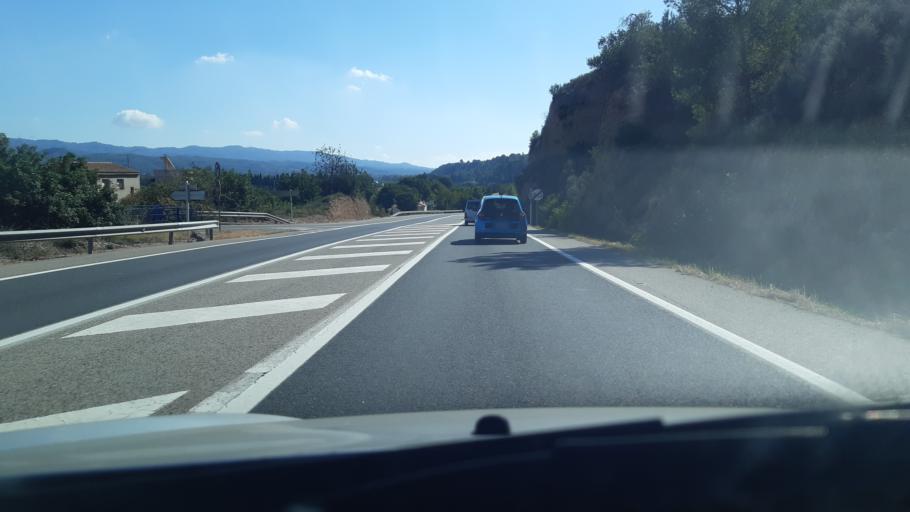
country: ES
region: Catalonia
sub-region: Provincia de Tarragona
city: Tivenys
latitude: 40.8773
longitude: 0.5001
